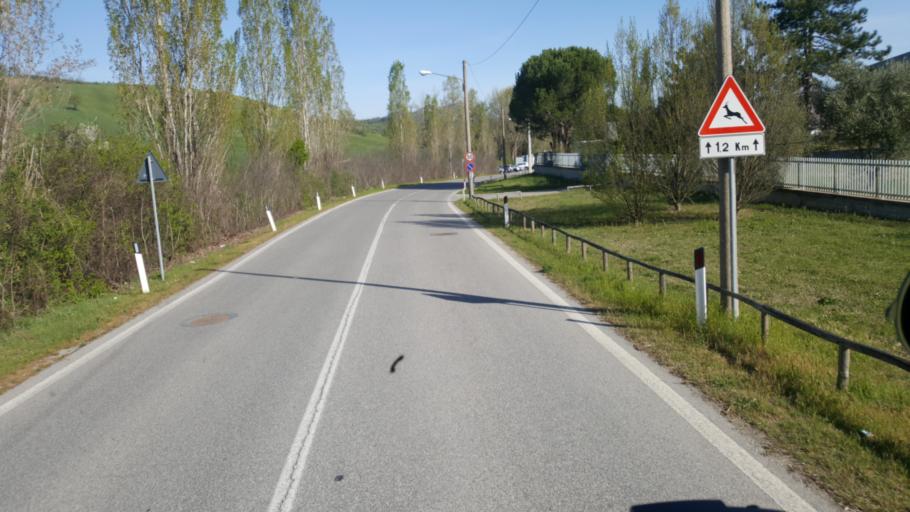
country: SM
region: Acquaviva
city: Acquaviva
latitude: 43.9428
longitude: 12.4061
